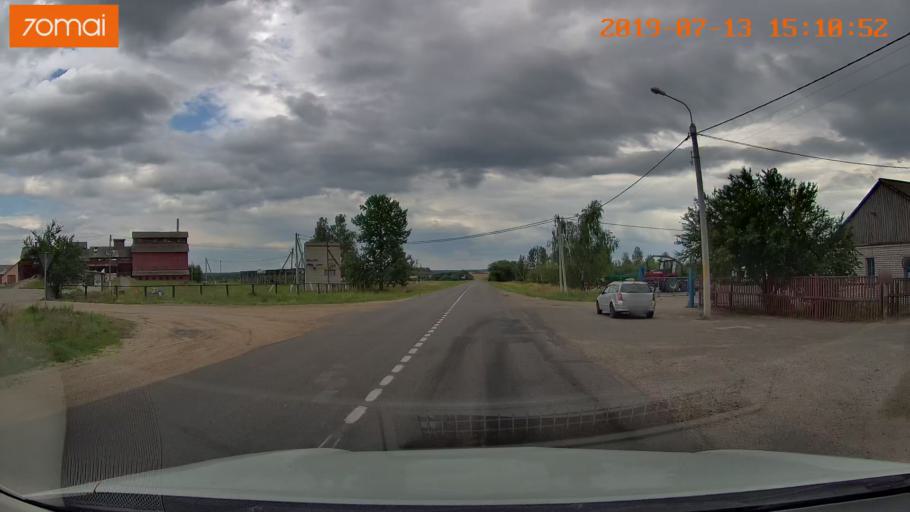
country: BY
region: Mogilev
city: Hlusha
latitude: 53.1680
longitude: 28.7796
